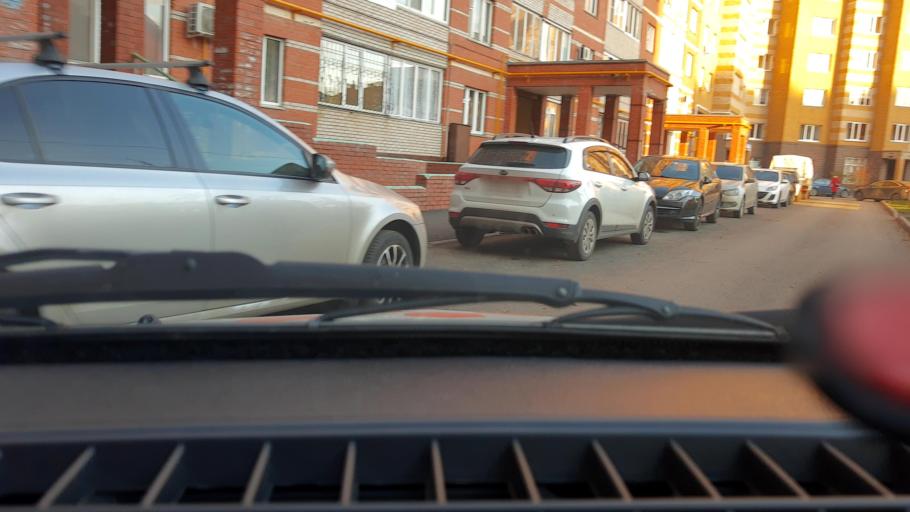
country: RU
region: Bashkortostan
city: Ufa
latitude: 54.7801
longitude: 56.0760
